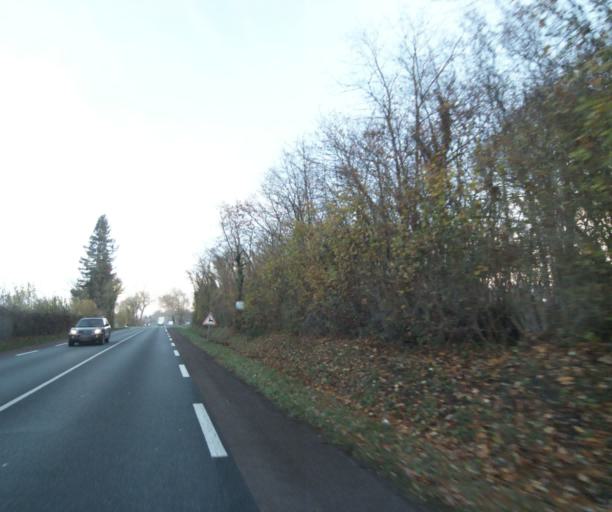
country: FR
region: Poitou-Charentes
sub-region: Departement de la Charente-Maritime
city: Fontcouverte
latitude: 45.7546
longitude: -0.5944
